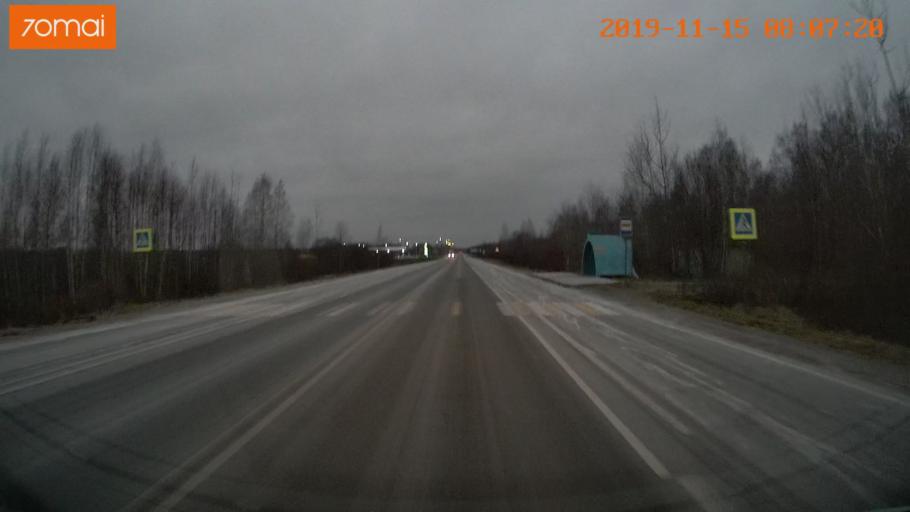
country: RU
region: Vologda
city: Cherepovets
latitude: 59.0261
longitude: 38.0182
